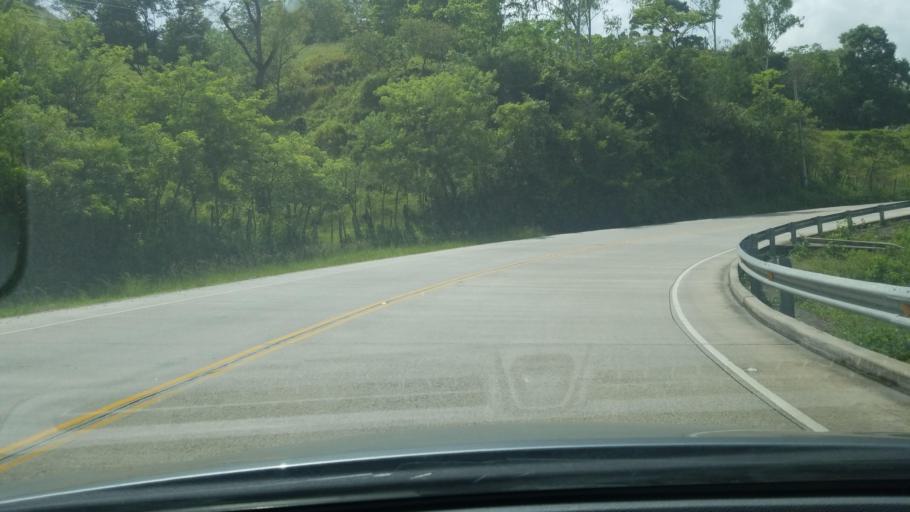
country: HN
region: Copan
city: San Jeronimo
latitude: 14.9581
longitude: -88.9068
